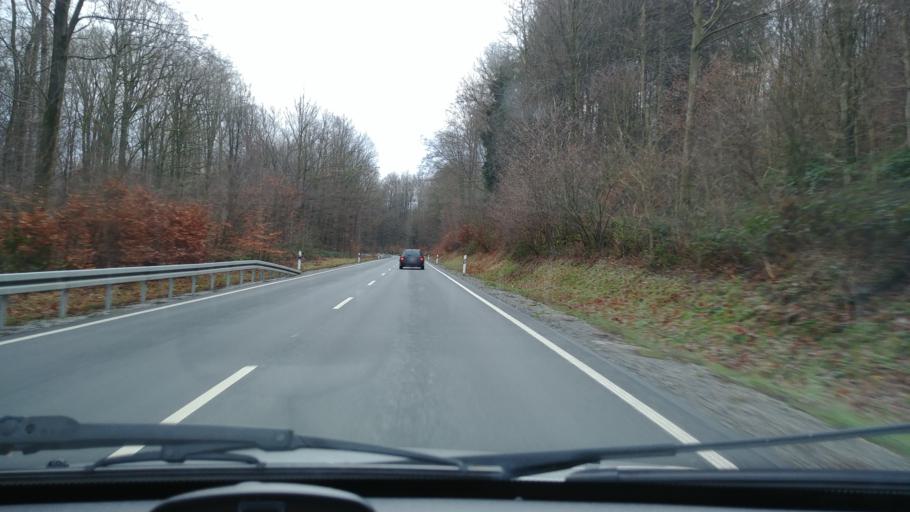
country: DE
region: Bavaria
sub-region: Regierungsbezirk Unterfranken
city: Rothenbuch
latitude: 49.9878
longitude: 9.3903
